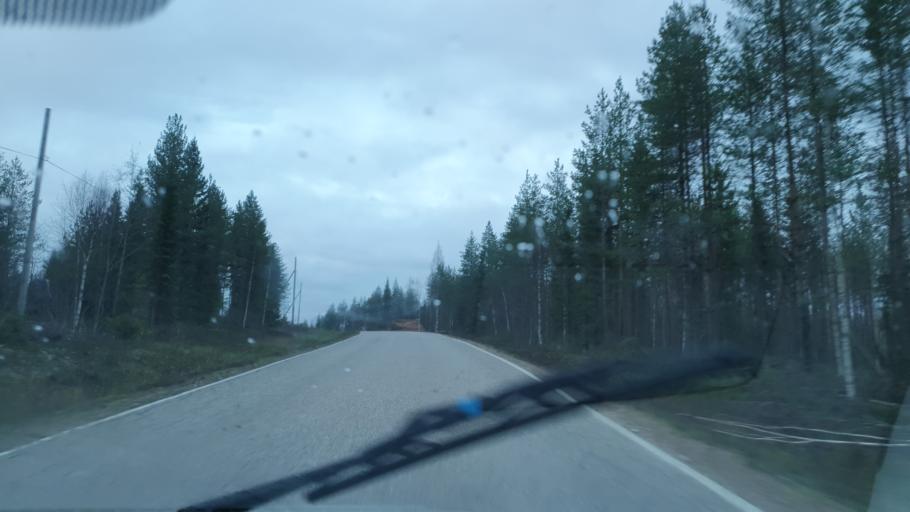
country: FI
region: Kainuu
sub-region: Kajaani
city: Ristijaervi
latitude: 64.4396
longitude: 28.3699
